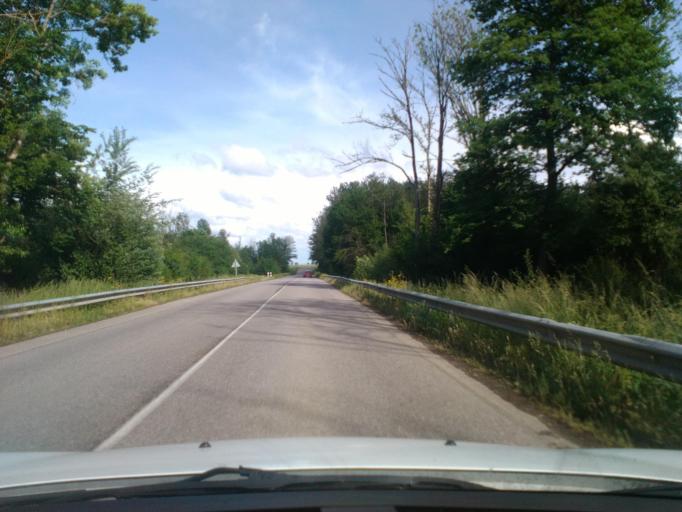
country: FR
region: Lorraine
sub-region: Departement de Meurthe-et-Moselle
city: Baccarat
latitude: 48.5602
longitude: 6.6906
